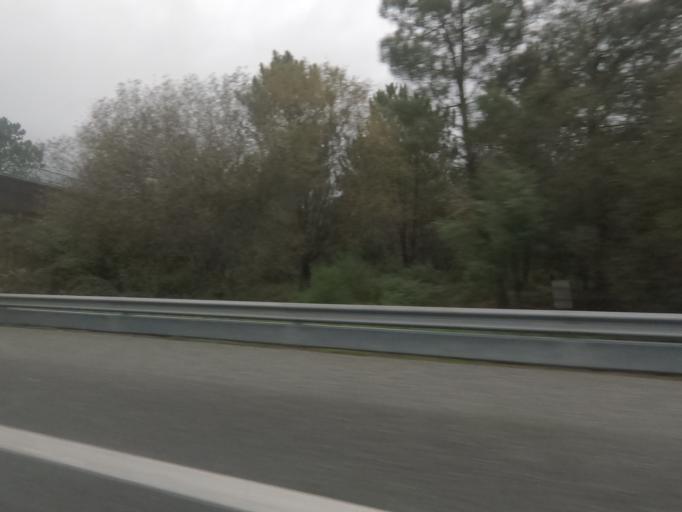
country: PT
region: Viana do Castelo
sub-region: Ponte de Lima
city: Ponte de Lima
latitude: 41.8009
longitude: -8.5826
